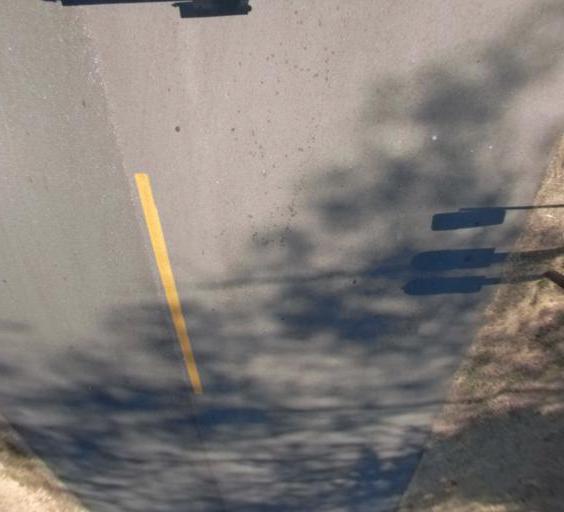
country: US
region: California
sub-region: Madera County
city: Bonadelle Ranchos-Madera Ranchos
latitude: 37.0017
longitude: -119.8829
